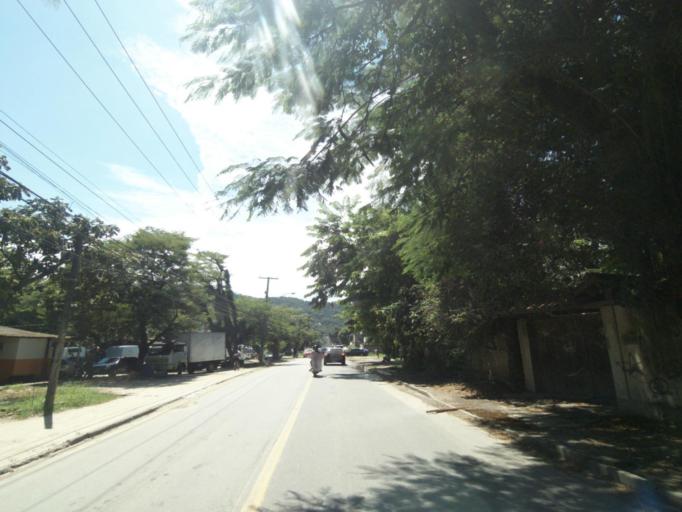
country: BR
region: Rio de Janeiro
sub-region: Niteroi
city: Niteroi
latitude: -22.9300
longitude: -43.0081
